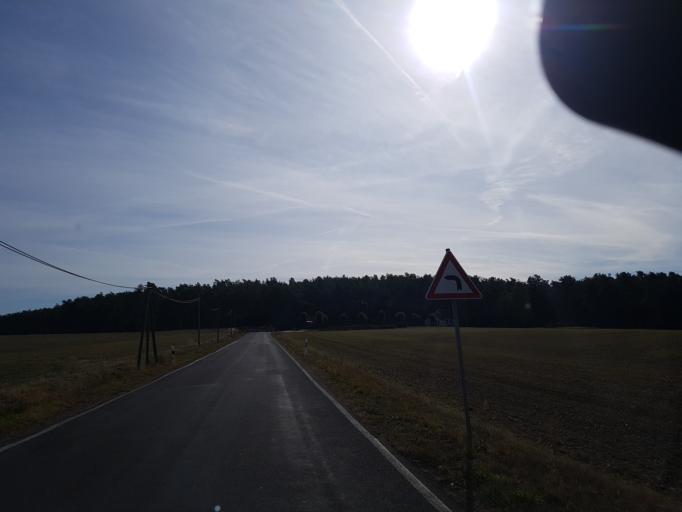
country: DE
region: Brandenburg
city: Schlieben
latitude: 51.6982
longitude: 13.4192
